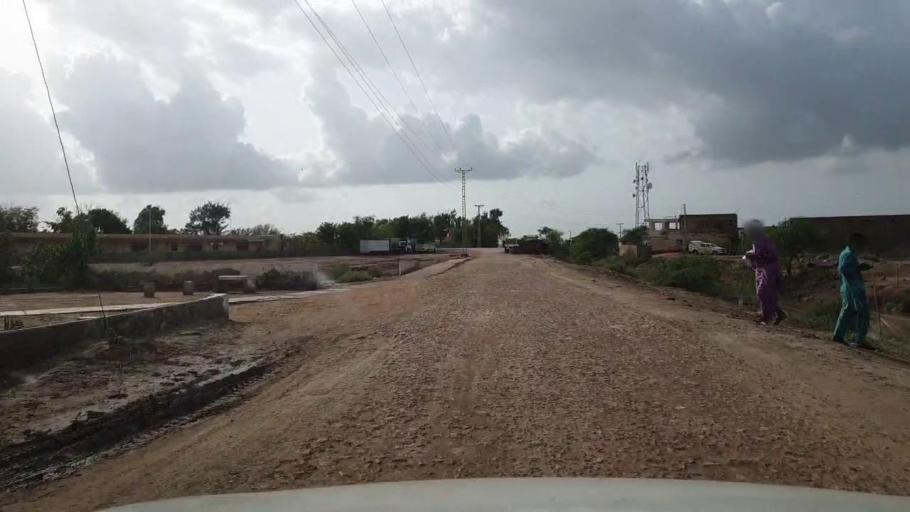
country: PK
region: Sindh
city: Kario
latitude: 24.7952
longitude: 68.5758
